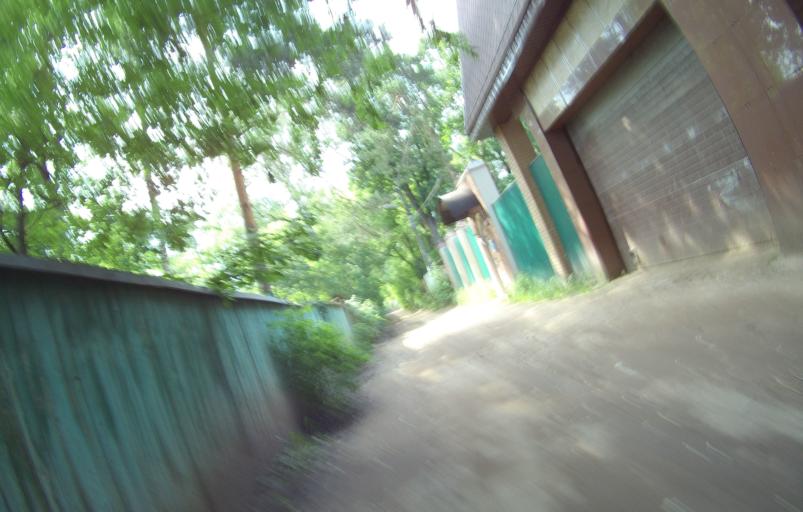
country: RU
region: Moskovskaya
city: Vereya
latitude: 55.6331
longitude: 38.0378
